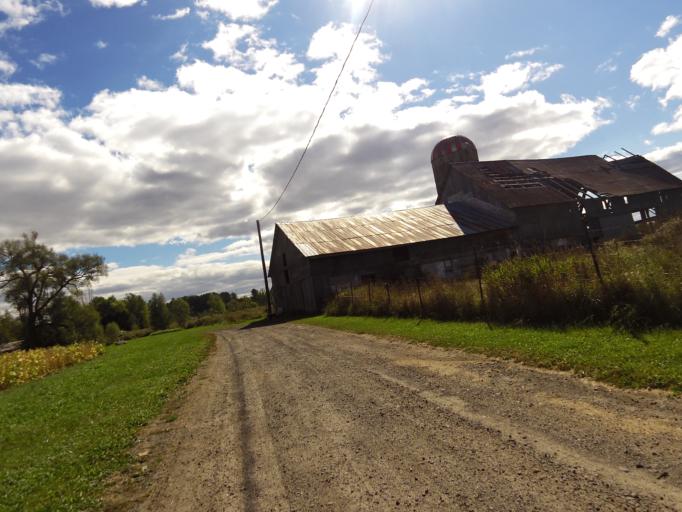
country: CA
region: Ontario
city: Ottawa
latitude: 45.3485
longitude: -75.5572
